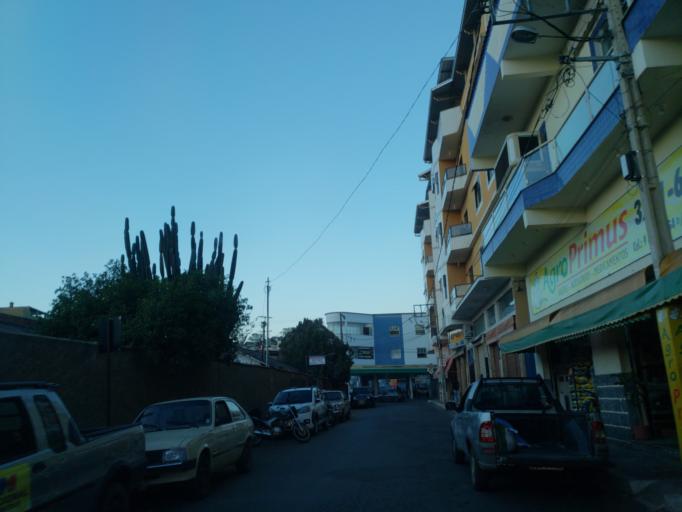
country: BR
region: Minas Gerais
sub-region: Sao Joao Nepomuceno
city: Sao Joao Nepomuceno
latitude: -21.5385
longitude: -43.0127
